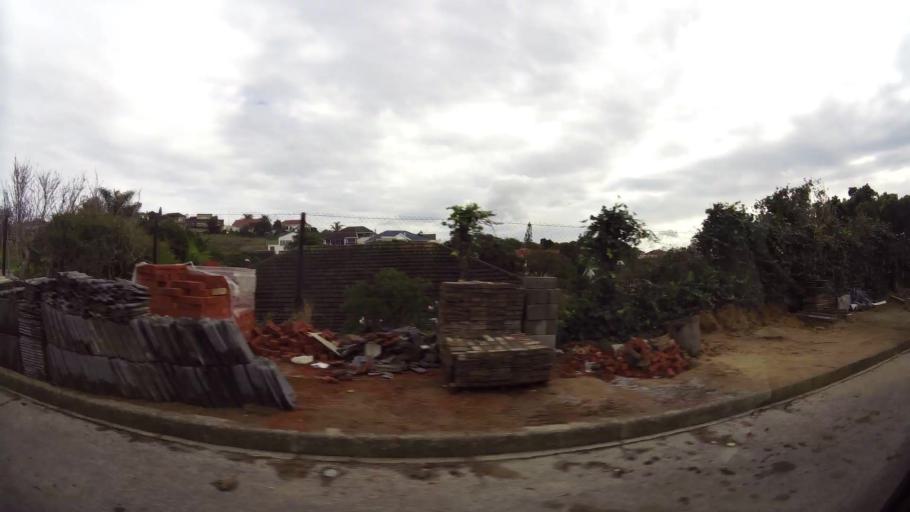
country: ZA
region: Eastern Cape
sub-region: Nelson Mandela Bay Metropolitan Municipality
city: Port Elizabeth
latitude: -33.9471
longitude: 25.5973
